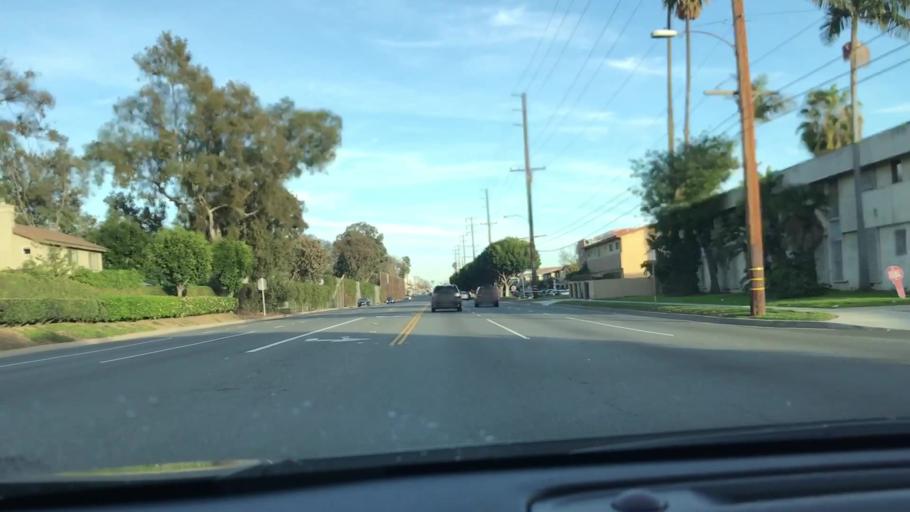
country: US
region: California
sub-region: Los Angeles County
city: West Athens
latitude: 33.9164
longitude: -118.3150
